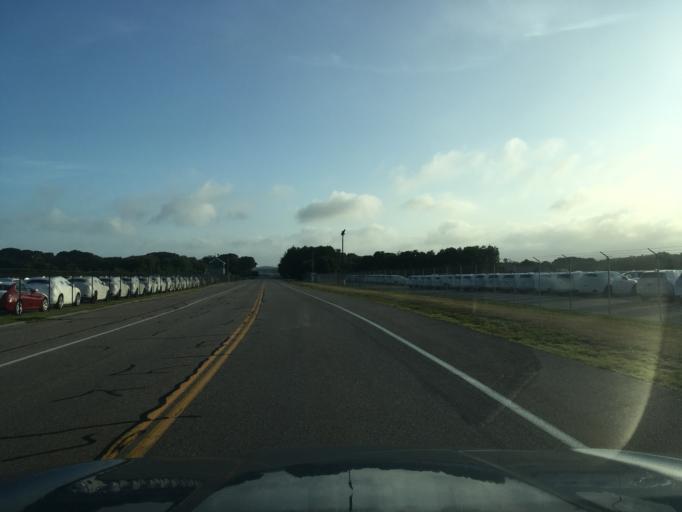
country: US
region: Rhode Island
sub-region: Kent County
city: East Greenwich
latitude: 41.6144
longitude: -71.4244
